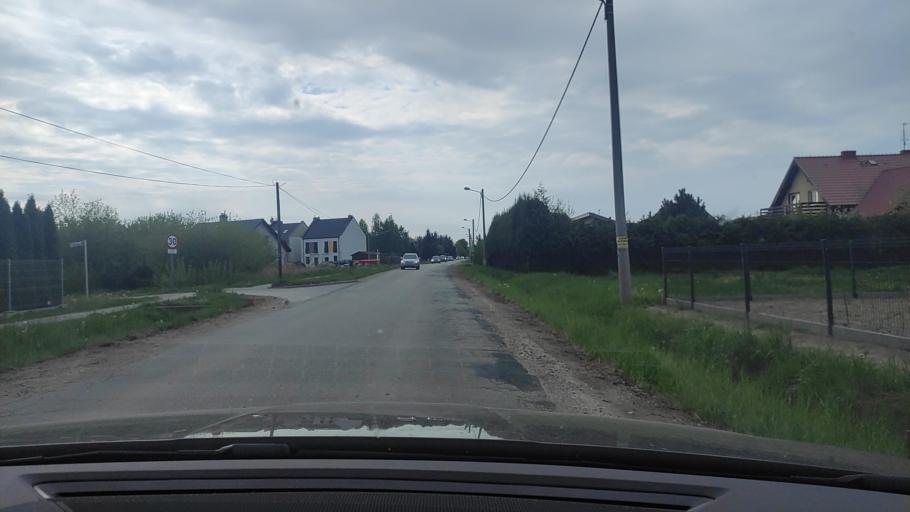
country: PL
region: Greater Poland Voivodeship
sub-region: Powiat poznanski
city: Kleszczewo
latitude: 52.3898
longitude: 17.1580
